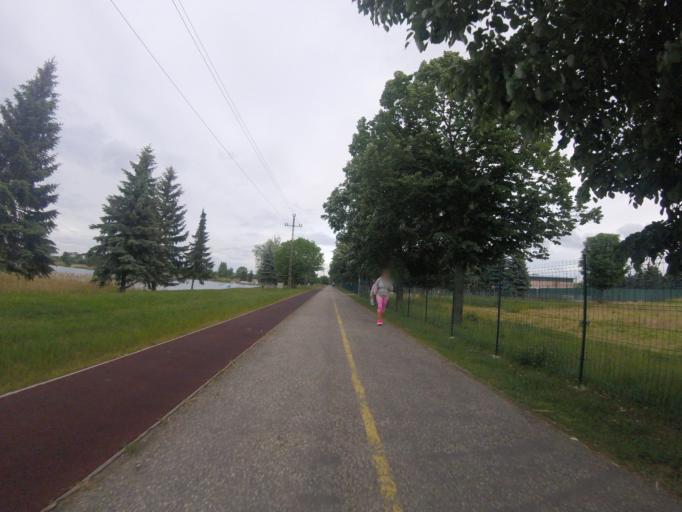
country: HU
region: Pest
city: Budakalasz
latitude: 47.6160
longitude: 19.0613
